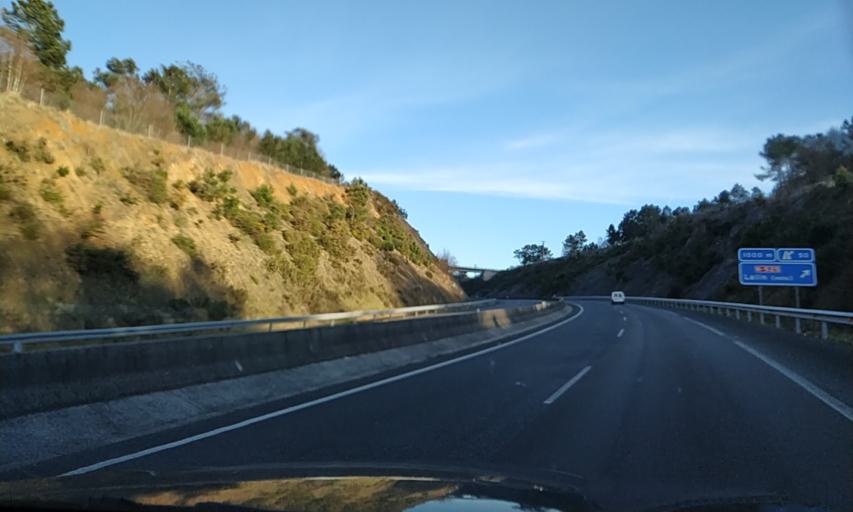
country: ES
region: Galicia
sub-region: Provincia de Pontevedra
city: Lalin
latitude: 42.6257
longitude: -8.1151
